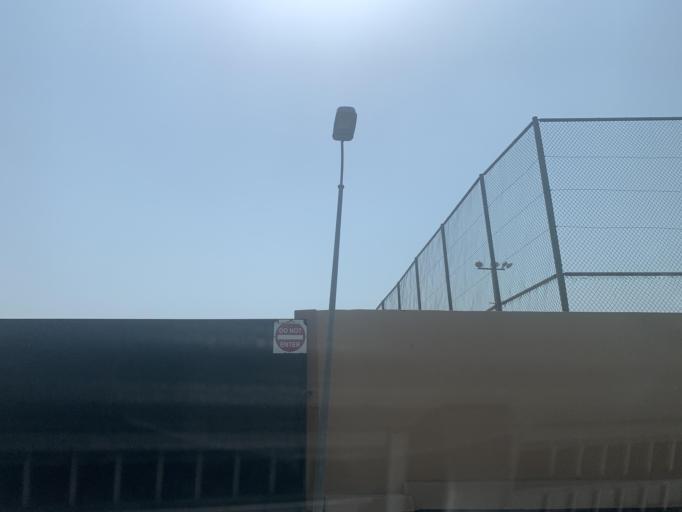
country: BH
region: Manama
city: Jidd Hafs
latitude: 26.2005
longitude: 50.4880
